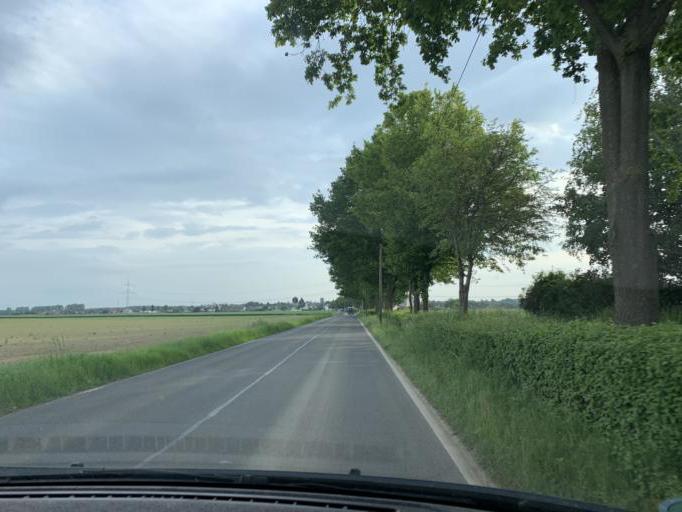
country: DE
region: North Rhine-Westphalia
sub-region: Regierungsbezirk Koln
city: Merzenich
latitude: 50.8167
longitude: 6.5123
